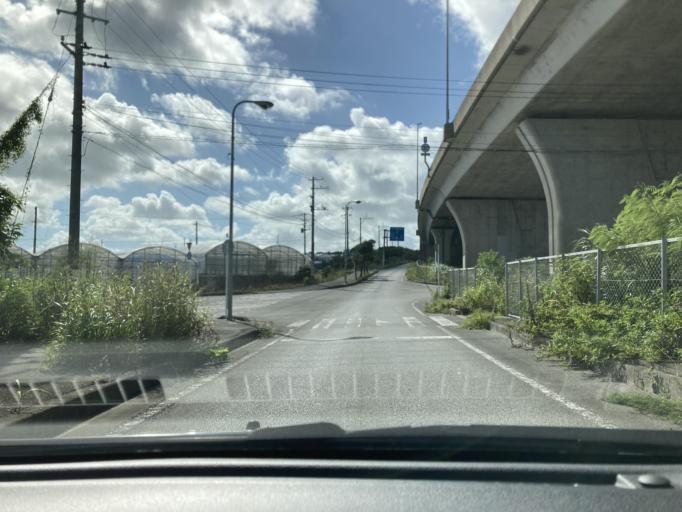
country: JP
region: Okinawa
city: Tomigusuku
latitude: 26.1809
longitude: 127.7290
